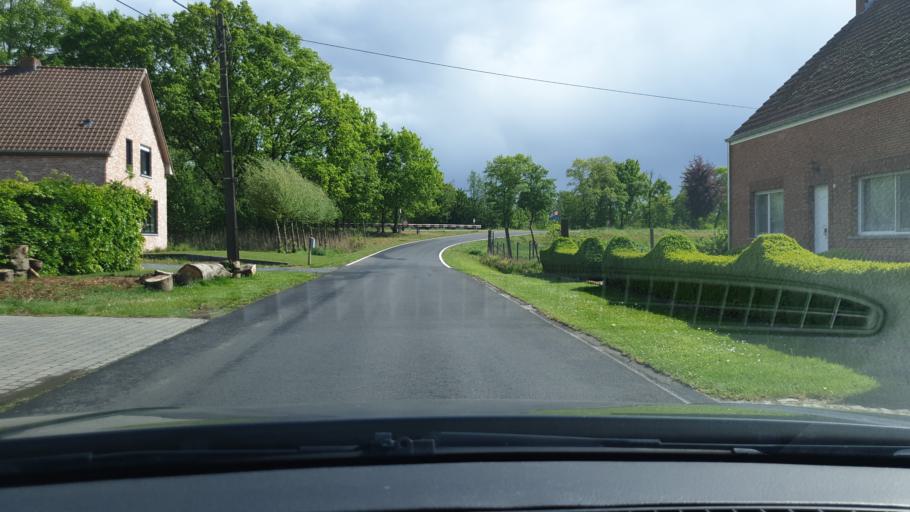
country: BE
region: Flanders
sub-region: Provincie Antwerpen
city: Geel
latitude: 51.1985
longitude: 4.9636
